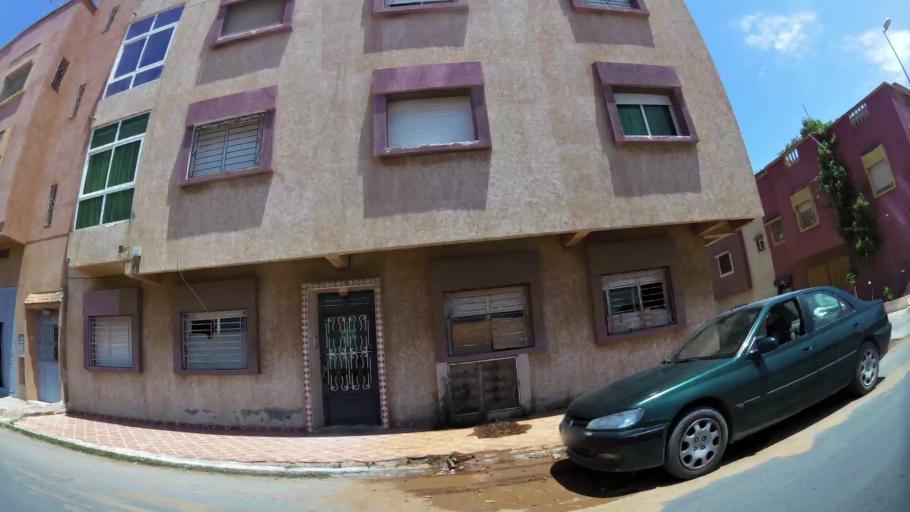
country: MA
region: Gharb-Chrarda-Beni Hssen
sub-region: Kenitra Province
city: Kenitra
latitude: 34.2486
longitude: -6.6236
